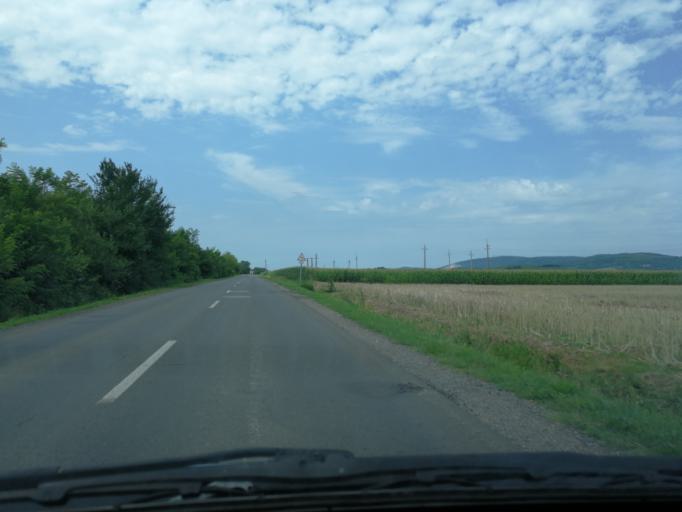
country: HU
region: Baranya
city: Siklos
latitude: 45.8496
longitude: 18.3530
